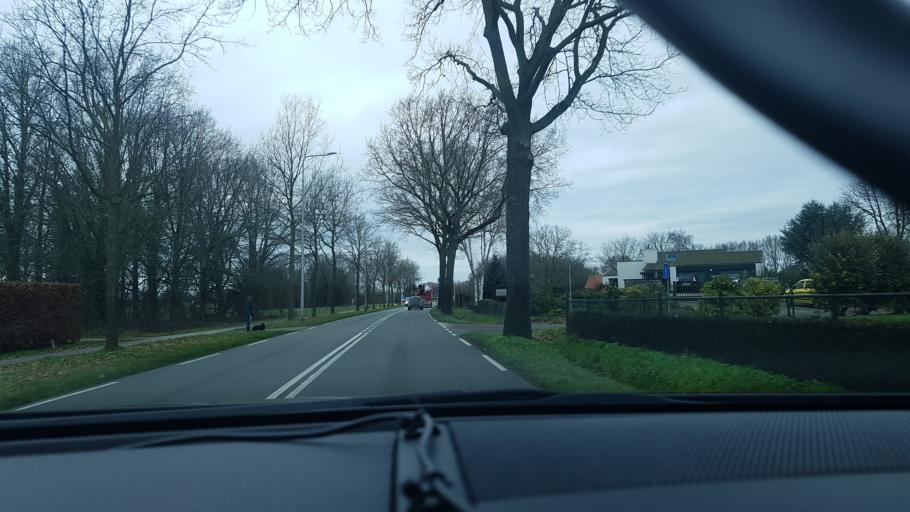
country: NL
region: Limburg
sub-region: Gemeente Leudal
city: Heythuysen
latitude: 51.2682
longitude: 5.9176
